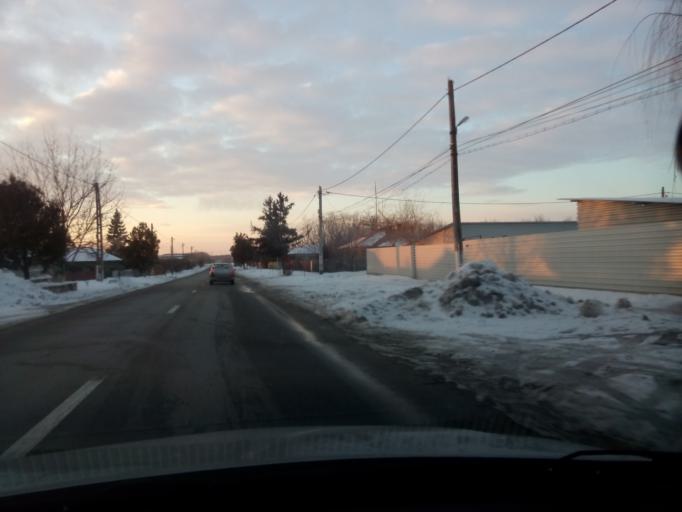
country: RO
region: Calarasi
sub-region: Comuna Soldanu
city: Soldanu
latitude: 44.2242
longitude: 26.5156
